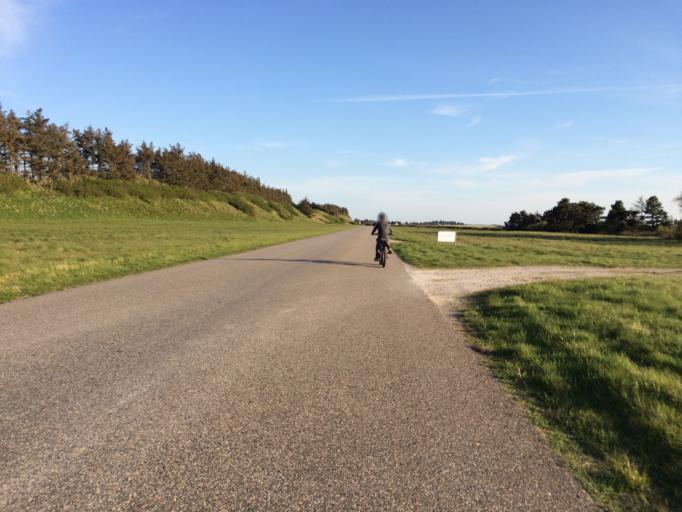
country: DK
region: Central Jutland
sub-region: Struer Kommune
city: Struer
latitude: 56.5332
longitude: 8.6276
